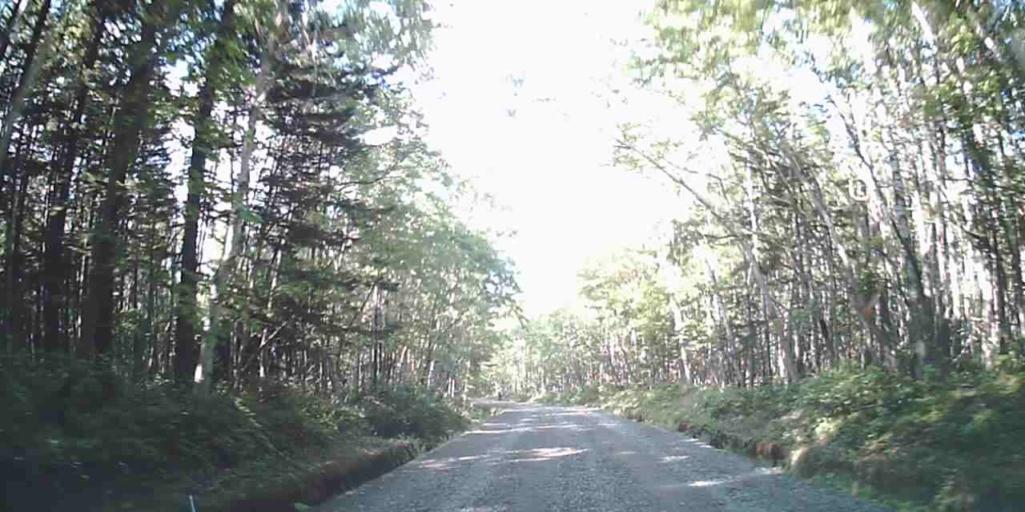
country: JP
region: Hokkaido
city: Shiraoi
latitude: 42.7107
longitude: 141.3994
